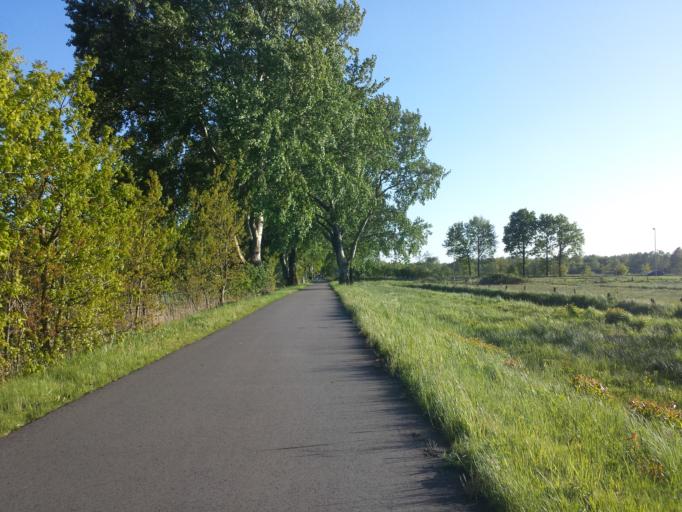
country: DE
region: Lower Saxony
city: Lilienthal
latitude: 53.1163
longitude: 8.8786
